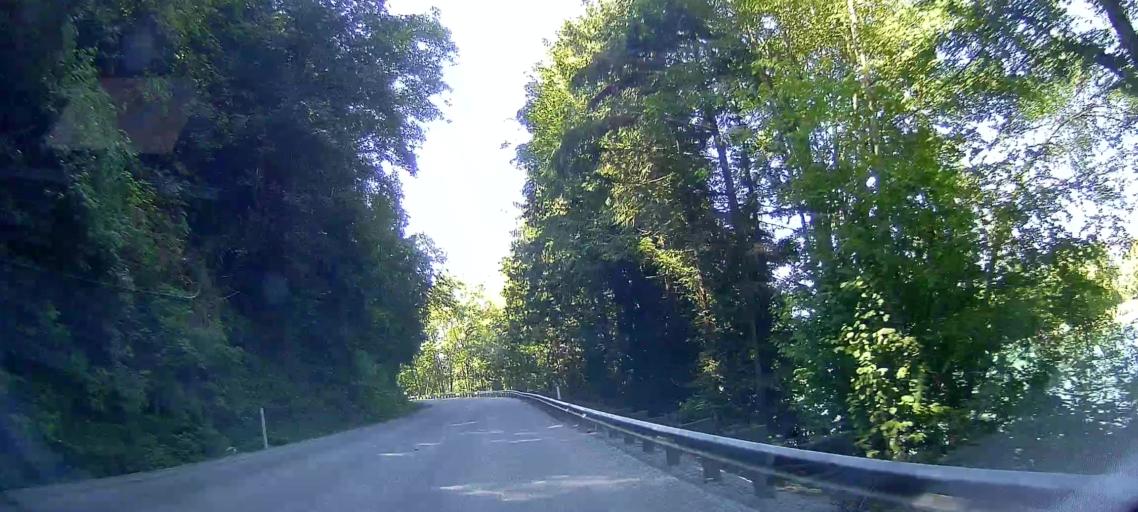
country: US
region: Washington
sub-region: Skagit County
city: Sedro-Woolley
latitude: 48.4873
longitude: -122.1941
